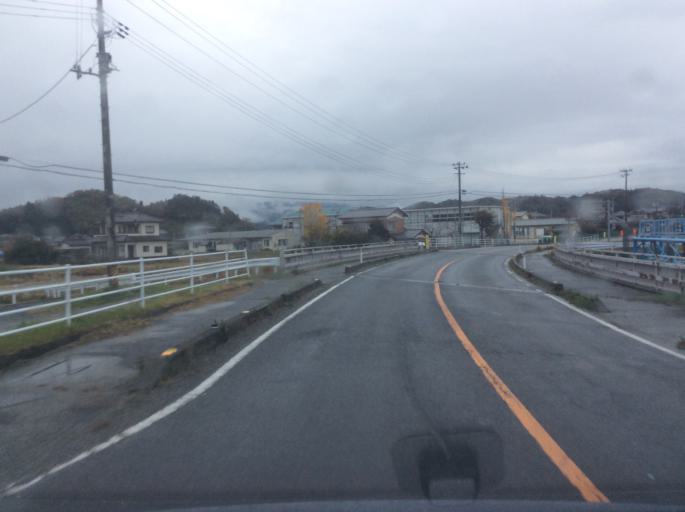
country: JP
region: Fukushima
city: Iwaki
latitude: 37.0790
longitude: 140.9529
